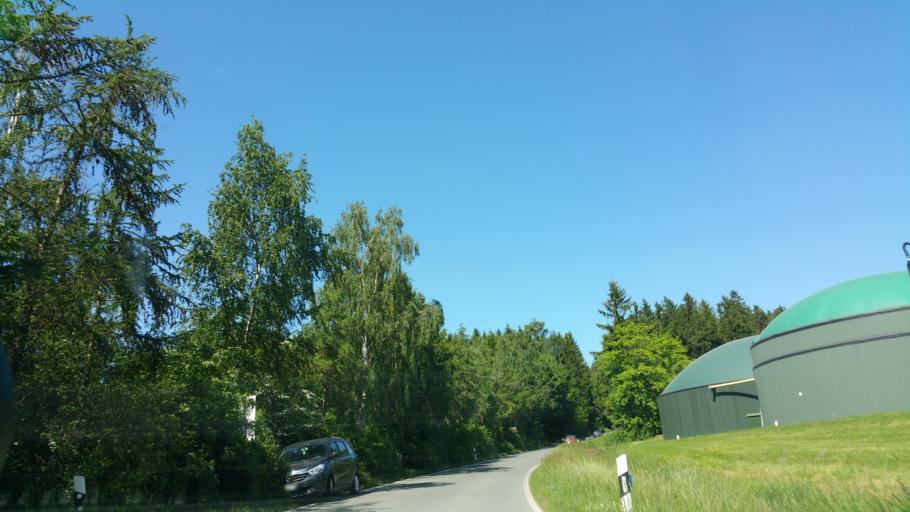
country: DE
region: Bavaria
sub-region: Upper Franconia
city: Schwarzenbach an der Saale
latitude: 50.1966
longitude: 11.9213
